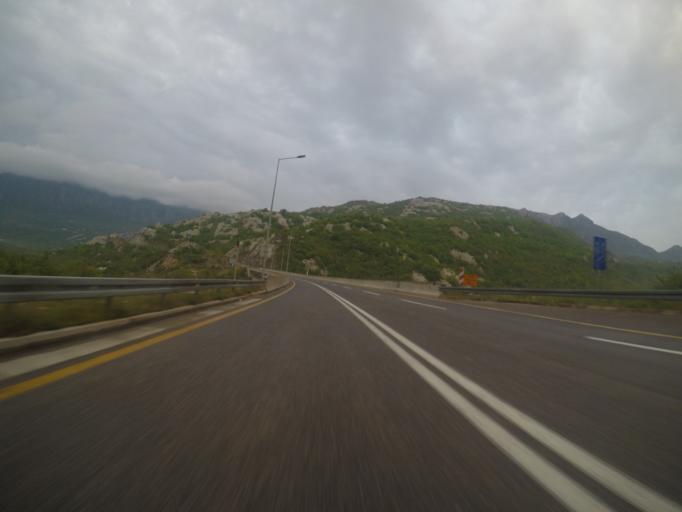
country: ME
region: Bar
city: Sutomore
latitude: 42.2264
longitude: 19.0527
